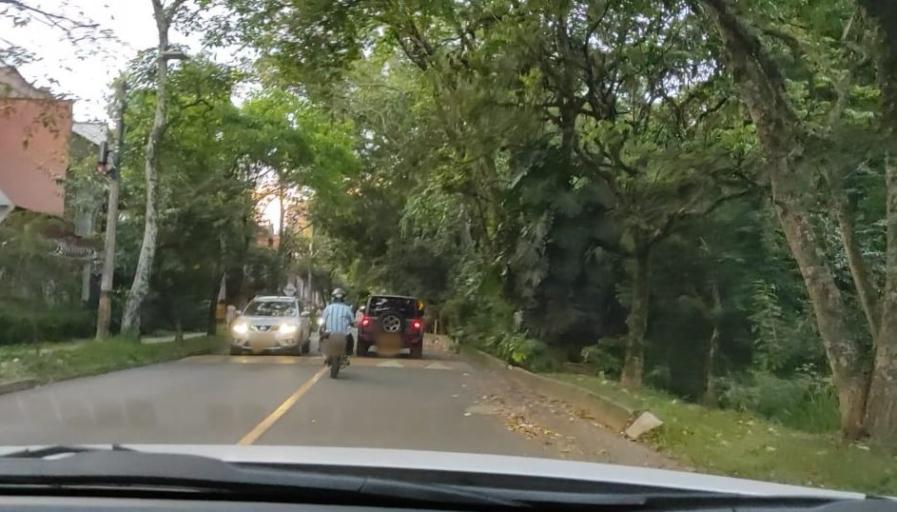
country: CO
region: Antioquia
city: Envigado
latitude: 6.1632
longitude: -75.5806
